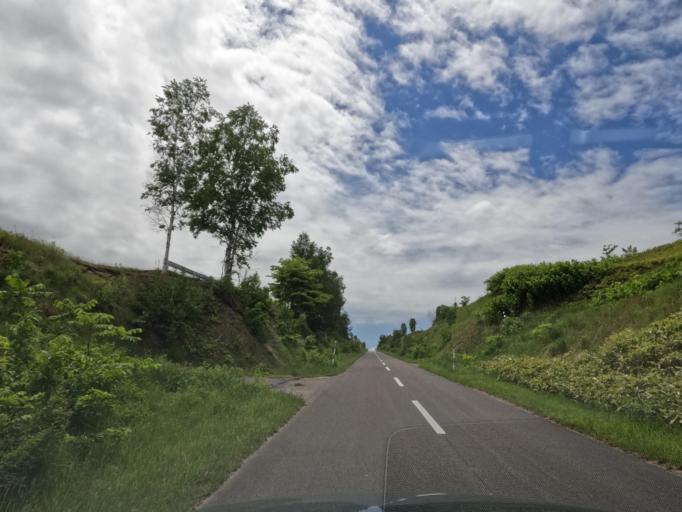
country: JP
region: Hokkaido
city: Shimo-furano
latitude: 43.5125
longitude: 142.4234
